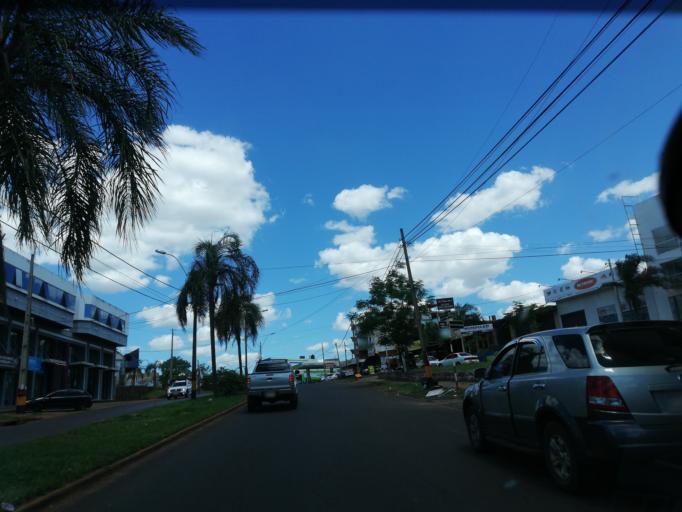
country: PY
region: Itapua
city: Encarnacion
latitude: -27.3551
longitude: -55.8561
